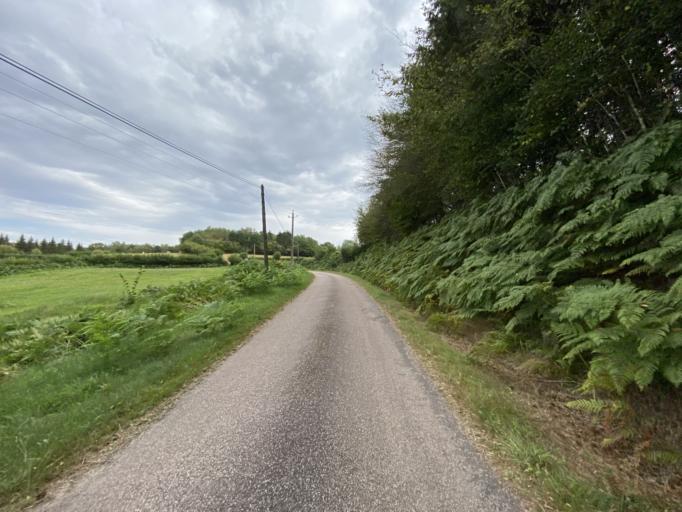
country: FR
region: Bourgogne
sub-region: Departement de la Cote-d'Or
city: Saulieu
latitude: 47.2617
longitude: 4.1365
